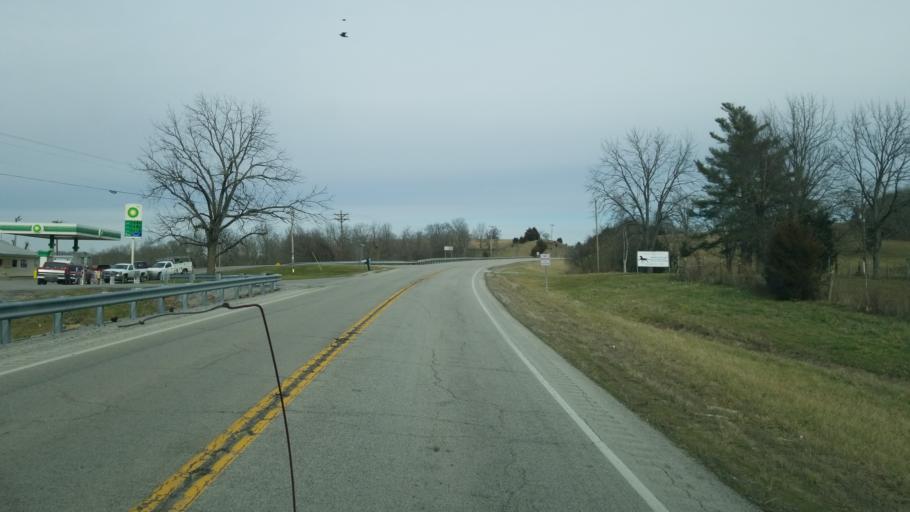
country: US
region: Kentucky
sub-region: Robertson County
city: Mount Olivet
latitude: 38.4367
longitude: -83.9910
